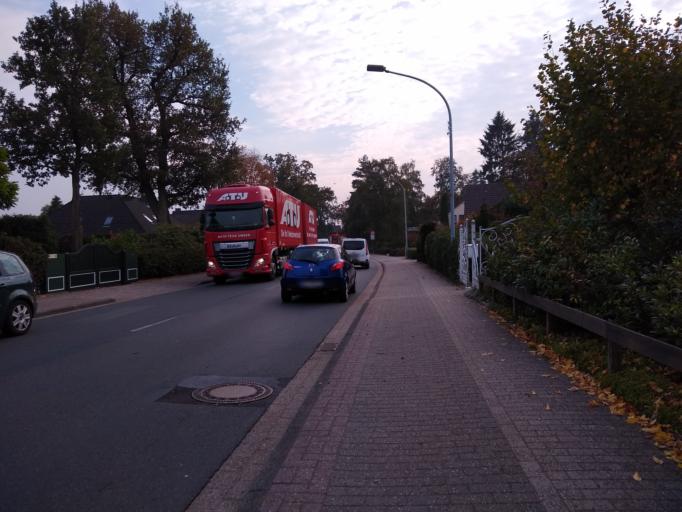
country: DE
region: Lower Saxony
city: Rastede
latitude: 53.2090
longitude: 8.2472
